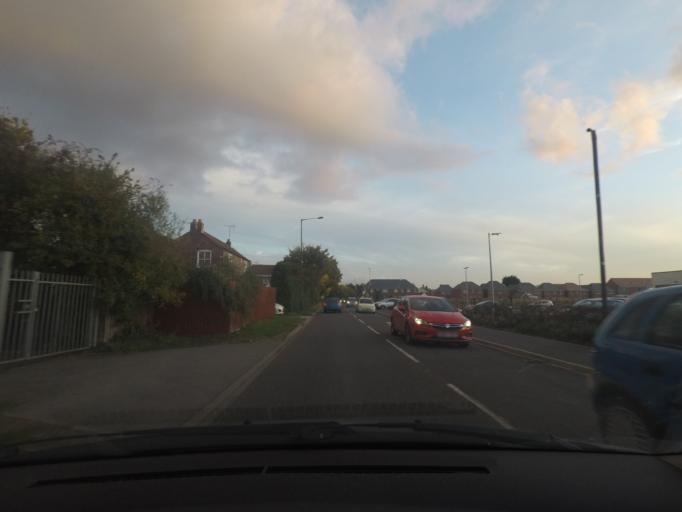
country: GB
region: England
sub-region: City of York
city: York
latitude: 53.9842
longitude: -1.0947
